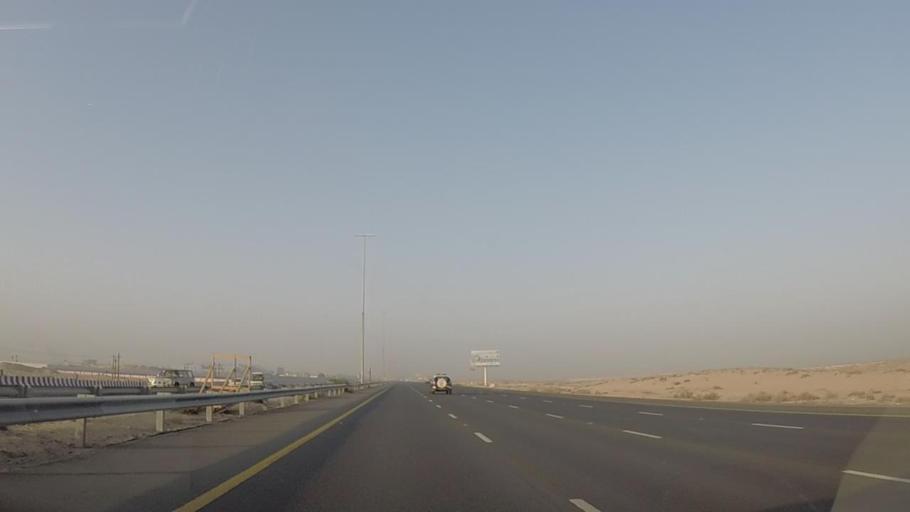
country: AE
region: Dubai
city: Dubai
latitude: 24.9298
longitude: 55.0124
